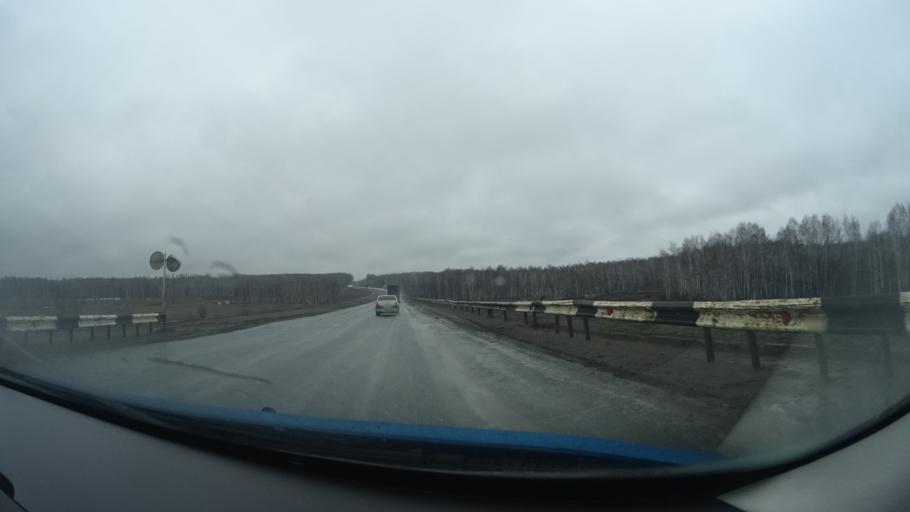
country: RU
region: Bashkortostan
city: Kandry
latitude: 54.5992
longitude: 54.2888
